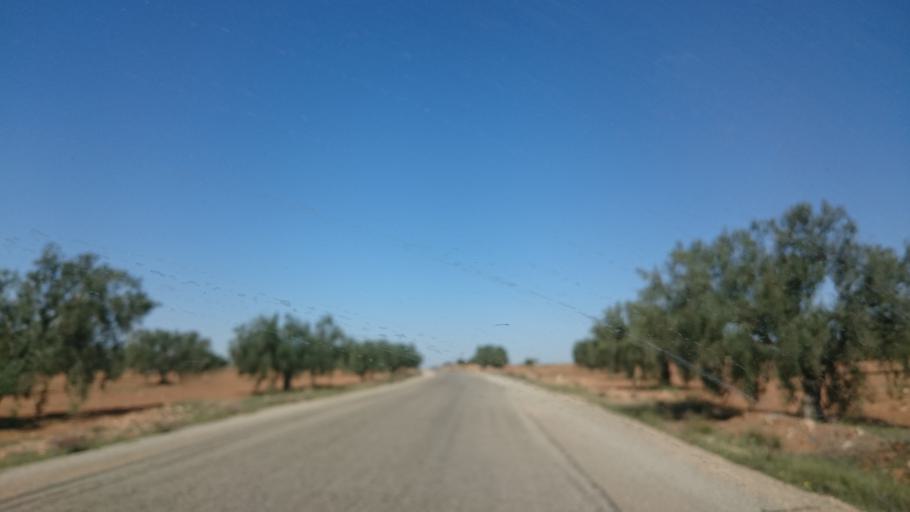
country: TN
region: Safaqis
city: Bi'r `Ali Bin Khalifah
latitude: 34.8697
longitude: 10.3942
